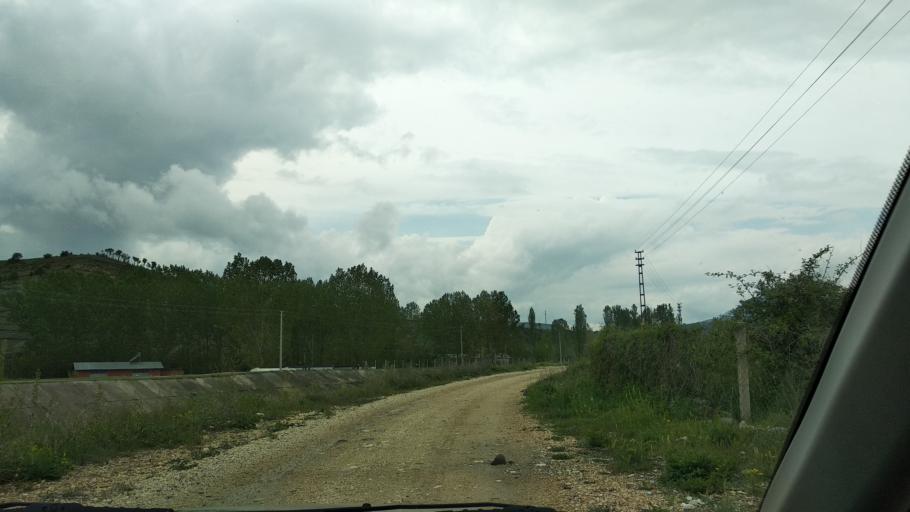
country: TR
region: Bolu
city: Seben
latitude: 40.4081
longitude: 31.5650
